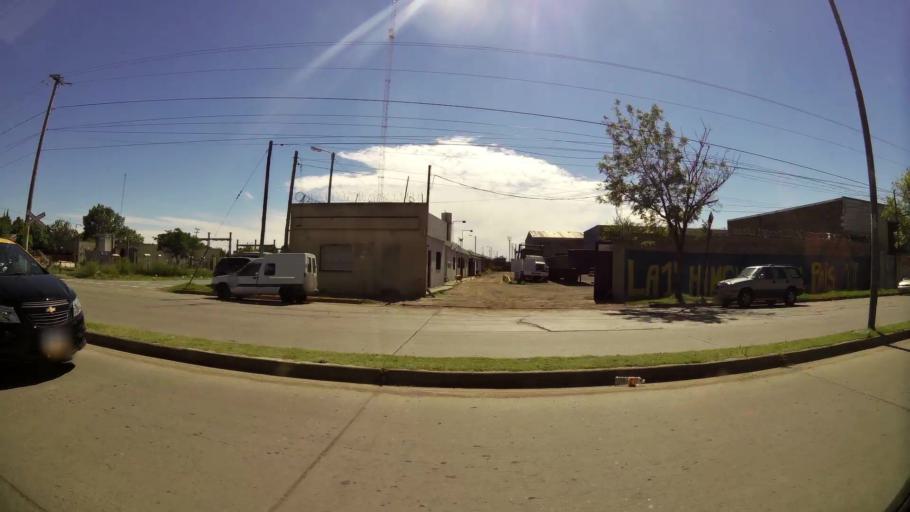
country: AR
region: Santa Fe
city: Granadero Baigorria
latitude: -32.9285
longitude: -60.7132
